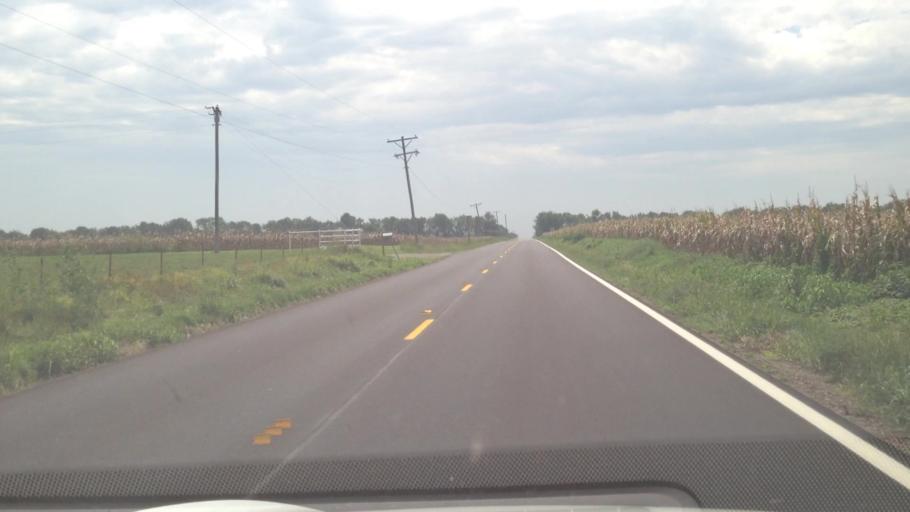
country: US
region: Kansas
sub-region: Crawford County
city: Girard
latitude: 37.6426
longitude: -94.9698
